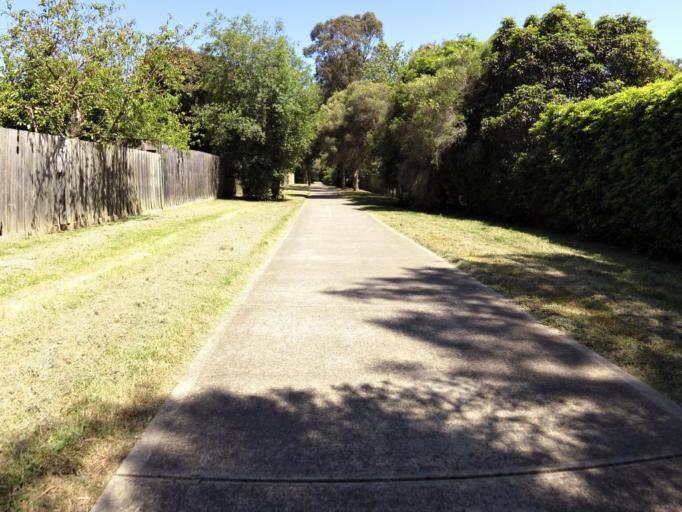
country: AU
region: Victoria
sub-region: Casey
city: Narre Warren
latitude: -38.0352
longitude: 145.3182
